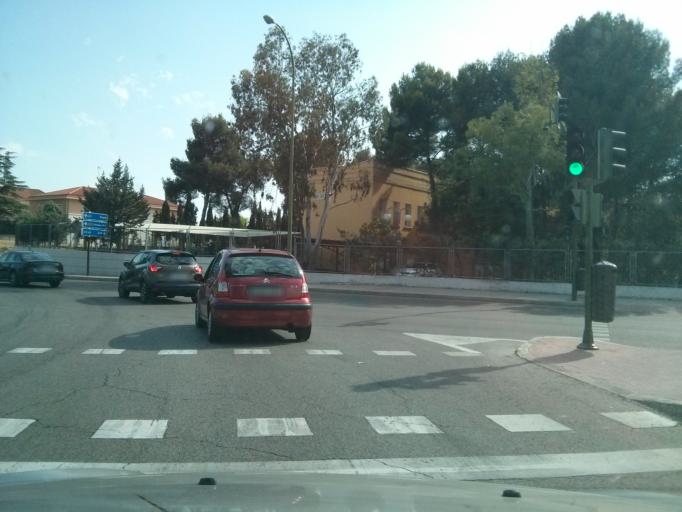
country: ES
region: Madrid
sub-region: Provincia de Madrid
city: Chamartin
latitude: 40.4754
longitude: -3.6895
